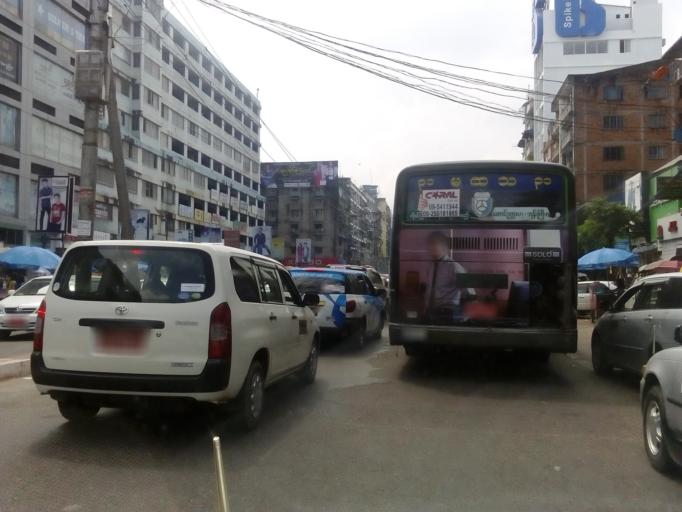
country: MM
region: Yangon
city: Yangon
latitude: 16.7946
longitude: 96.1757
